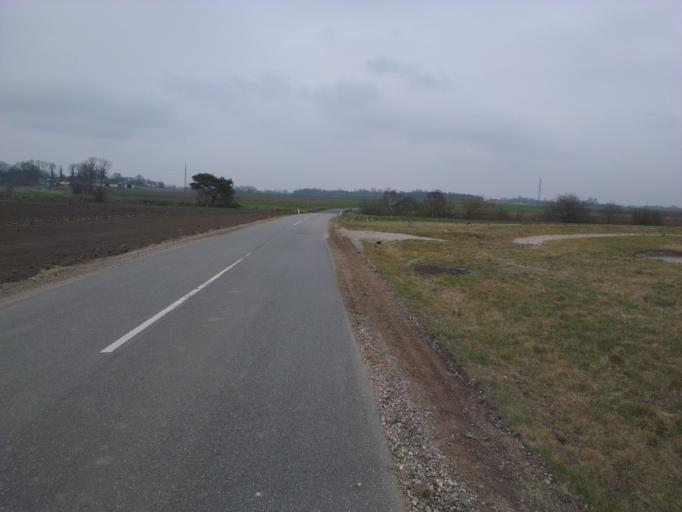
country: DK
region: Capital Region
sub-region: Frederikssund Kommune
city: Frederikssund
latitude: 55.8287
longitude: 12.1153
